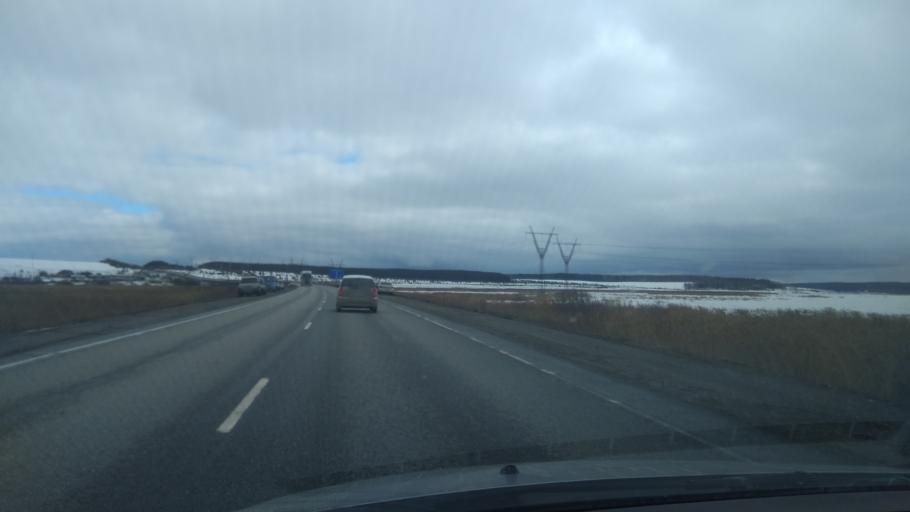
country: RU
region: Sverdlovsk
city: Achit
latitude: 56.7847
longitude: 57.8931
